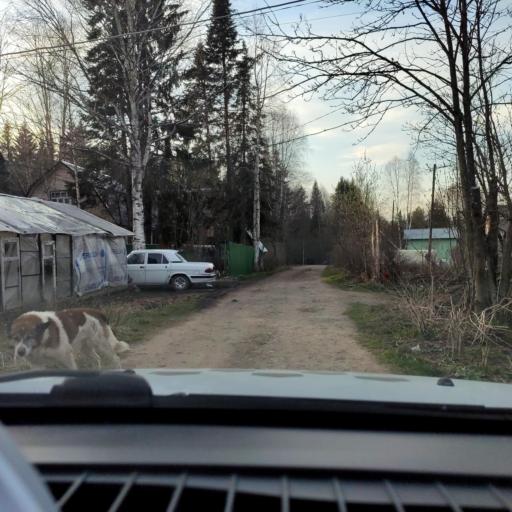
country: RU
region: Perm
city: Novyye Lyady
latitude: 58.0481
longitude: 56.6523
